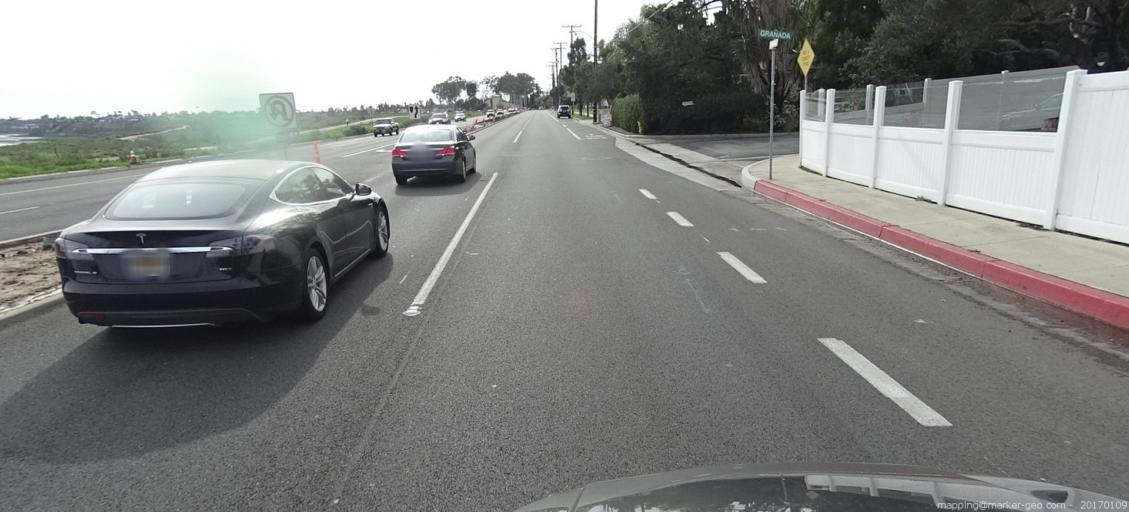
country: US
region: California
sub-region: Orange County
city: Costa Mesa
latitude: 33.6551
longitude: -117.8879
